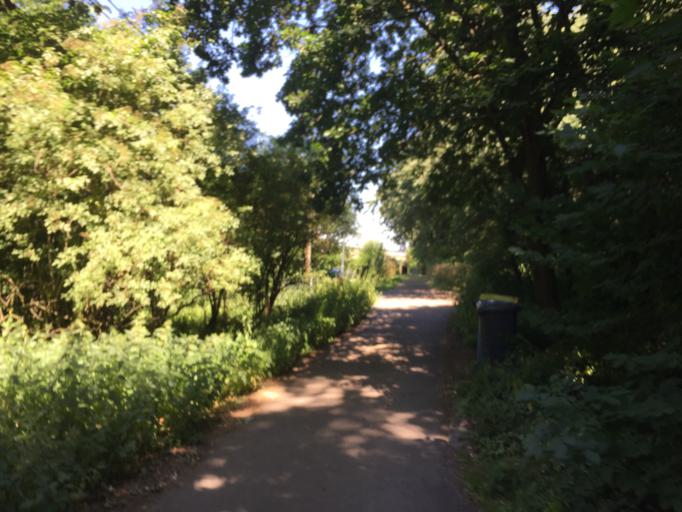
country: DE
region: Hesse
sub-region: Regierungsbezirk Giessen
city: Grossen Buseck
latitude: 50.5986
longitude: 8.8071
